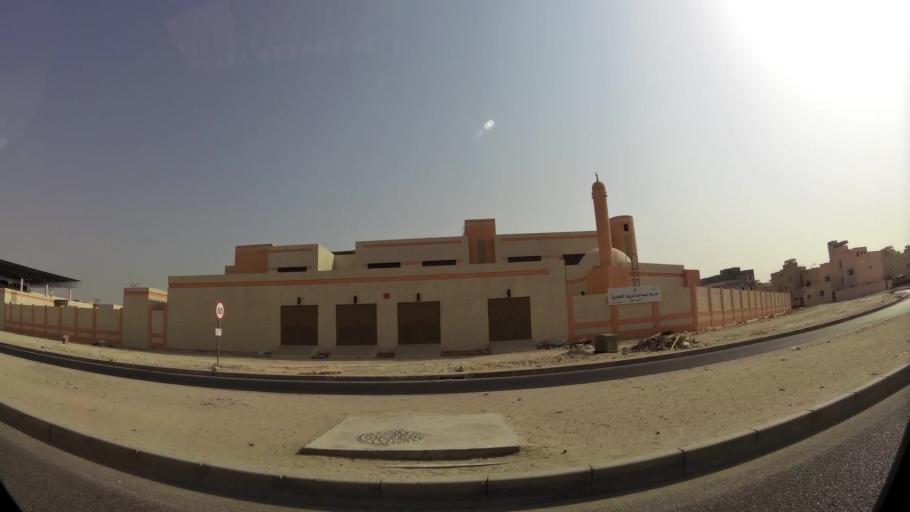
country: KW
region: Muhafazat al Jahra'
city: Al Jahra'
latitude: 29.3578
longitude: 47.7555
